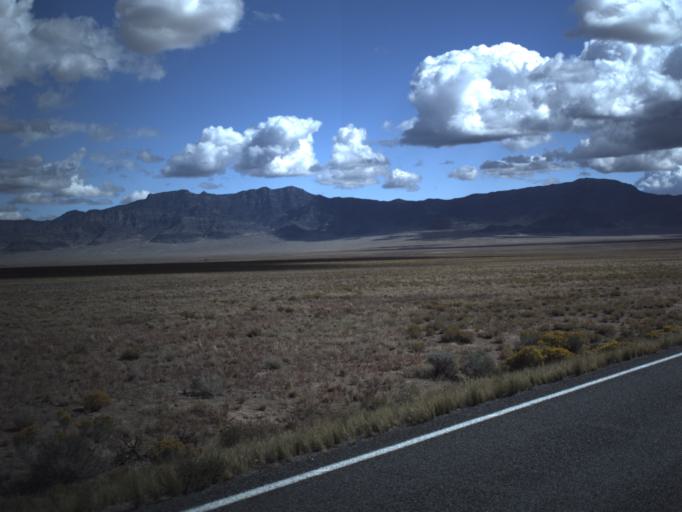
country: US
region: Utah
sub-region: Beaver County
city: Milford
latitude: 38.5565
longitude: -113.7475
